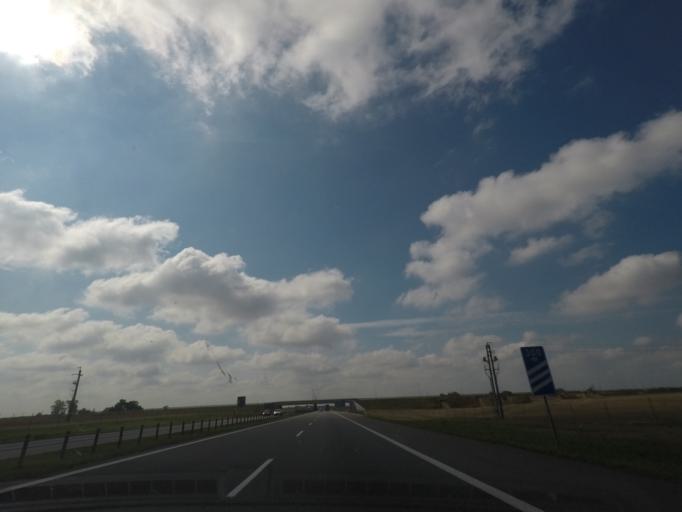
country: PL
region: Kujawsko-Pomorskie
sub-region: Powiat chelminski
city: Lisewo
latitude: 53.2953
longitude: 18.7072
